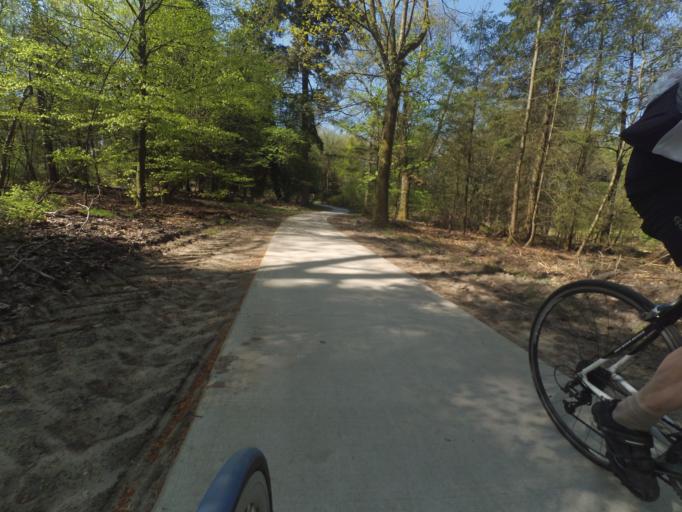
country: NL
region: Gelderland
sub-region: Gemeente Apeldoorn
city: Beekbergen
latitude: 52.1472
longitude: 5.8872
